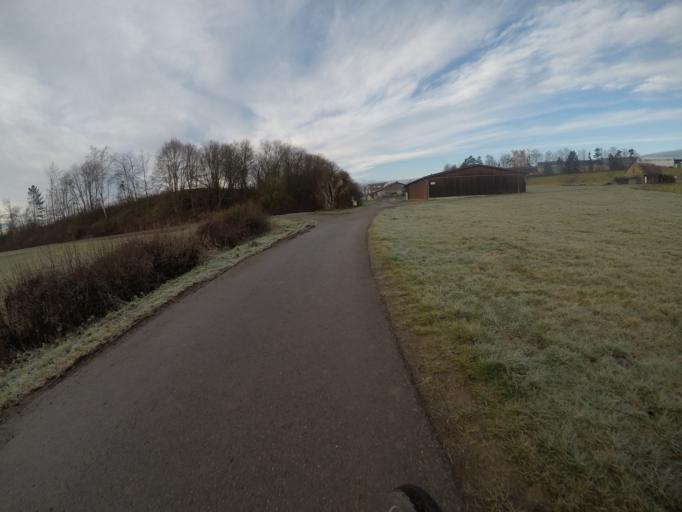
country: DE
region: Baden-Wuerttemberg
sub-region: Regierungsbezirk Stuttgart
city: Magstadt
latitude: 48.7022
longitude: 8.9517
